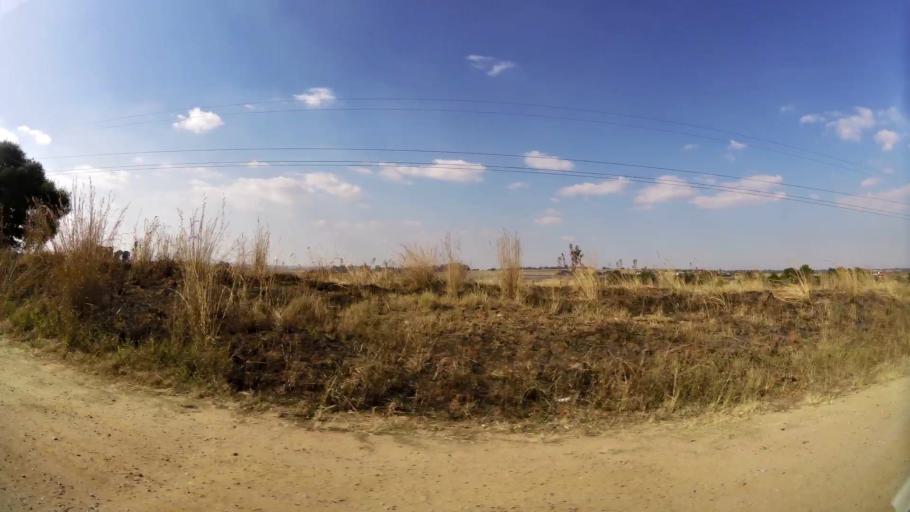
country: ZA
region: Gauteng
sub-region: Ekurhuleni Metropolitan Municipality
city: Tembisa
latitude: -26.0480
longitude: 28.2524
